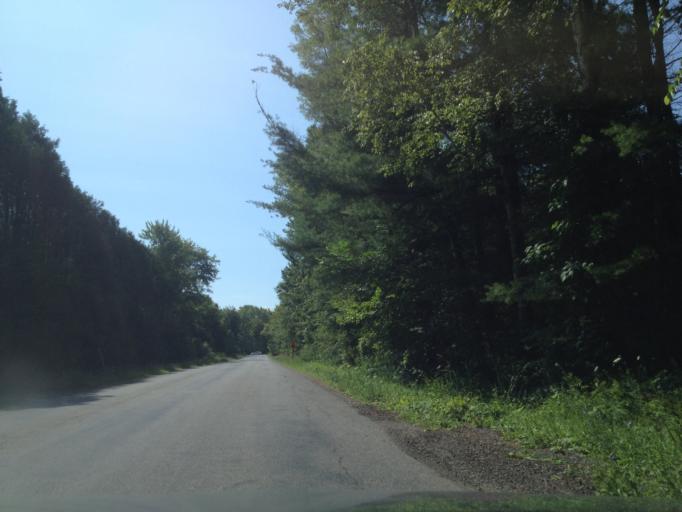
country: CA
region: Ontario
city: Norfolk County
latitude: 42.8155
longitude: -80.3771
